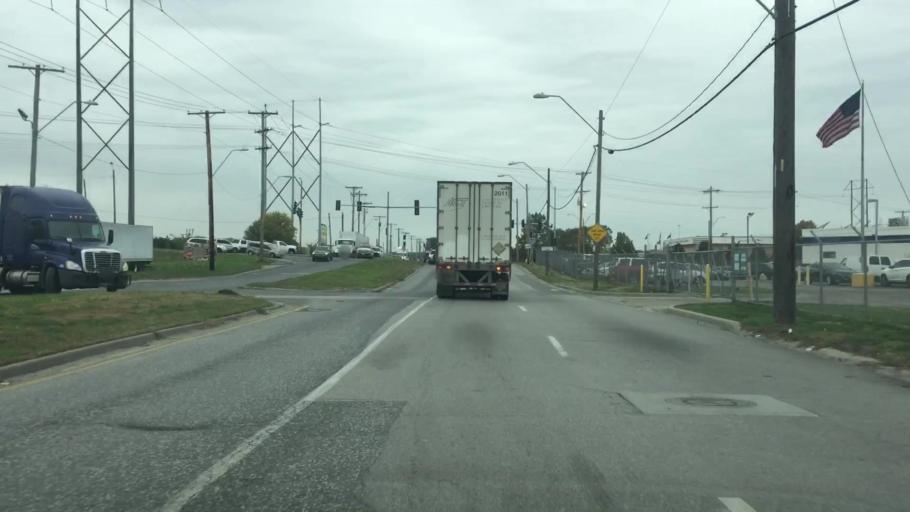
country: US
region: Missouri
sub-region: Clay County
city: North Kansas City
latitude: 39.1308
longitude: -94.5213
